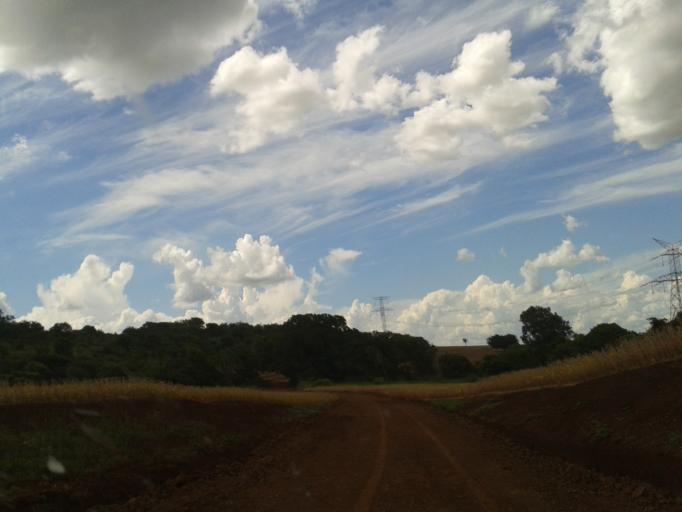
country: BR
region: Minas Gerais
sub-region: Capinopolis
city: Capinopolis
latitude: -18.7312
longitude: -49.7756
